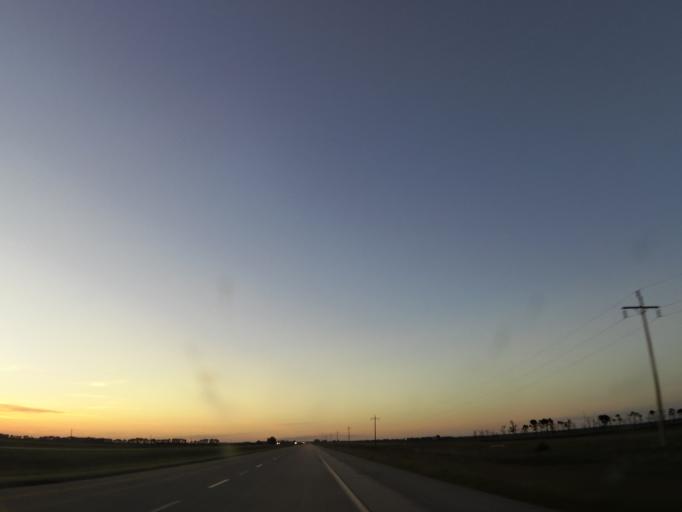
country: US
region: North Dakota
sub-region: Walsh County
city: Grafton
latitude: 48.3293
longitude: -97.1892
